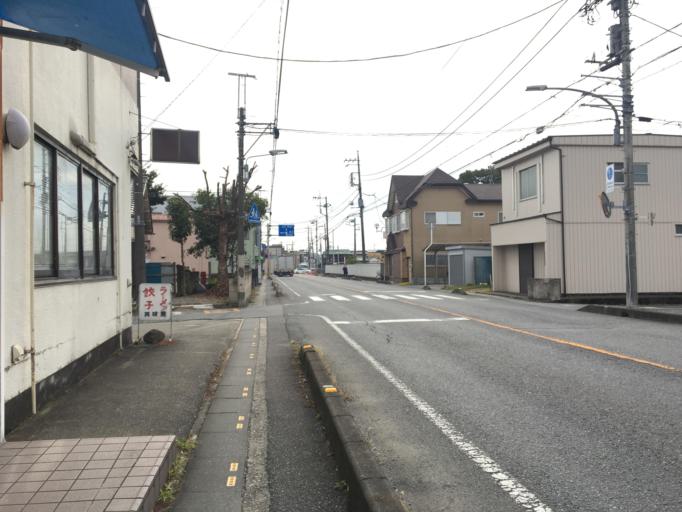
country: JP
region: Saitama
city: Yoshikawa
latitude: 35.8870
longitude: 139.8411
